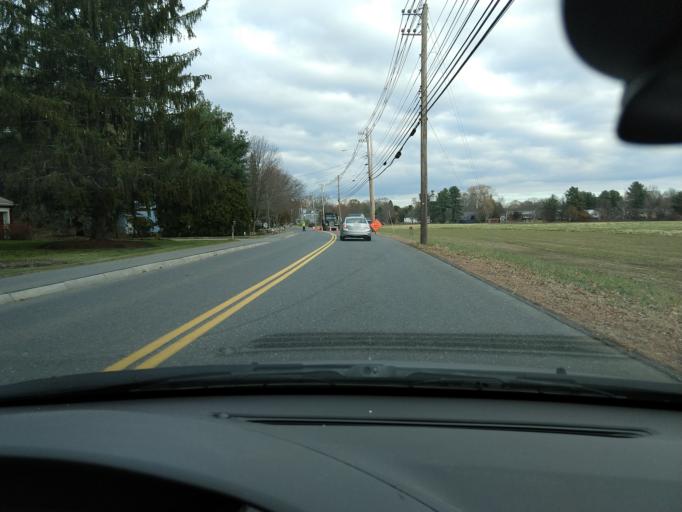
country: US
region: Massachusetts
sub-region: Middlesex County
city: Concord
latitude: 42.4630
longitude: -71.3224
